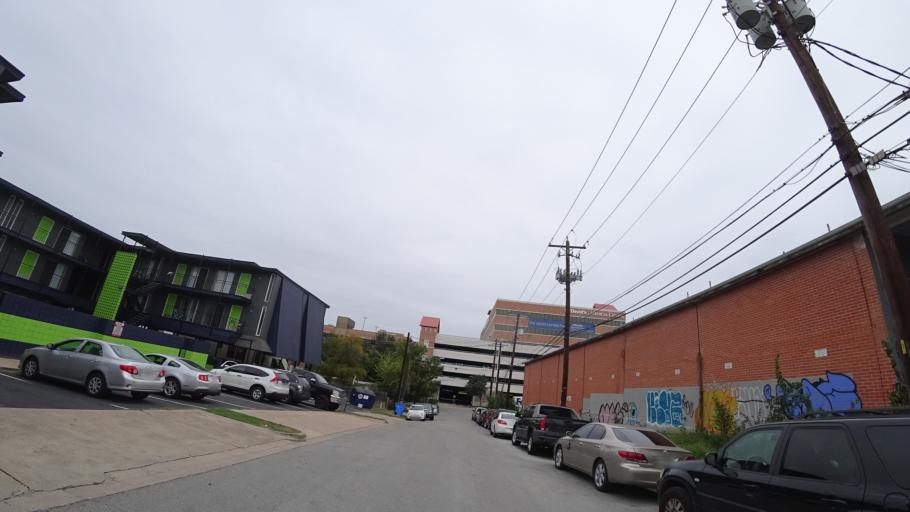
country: US
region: Texas
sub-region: Travis County
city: Austin
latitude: 30.2876
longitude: -97.7252
